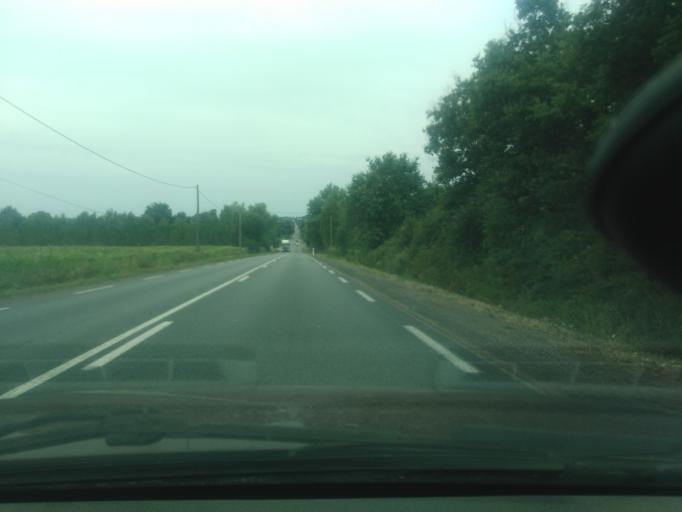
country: FR
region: Pays de la Loire
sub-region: Departement de la Vendee
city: Sainte-Cecile
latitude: 46.7610
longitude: -1.1027
